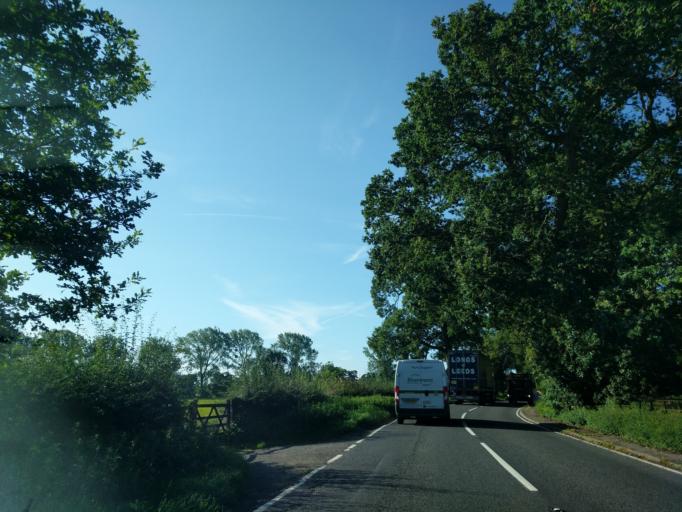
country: GB
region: England
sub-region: Lincolnshire
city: Bourne
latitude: 52.7934
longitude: -0.4446
